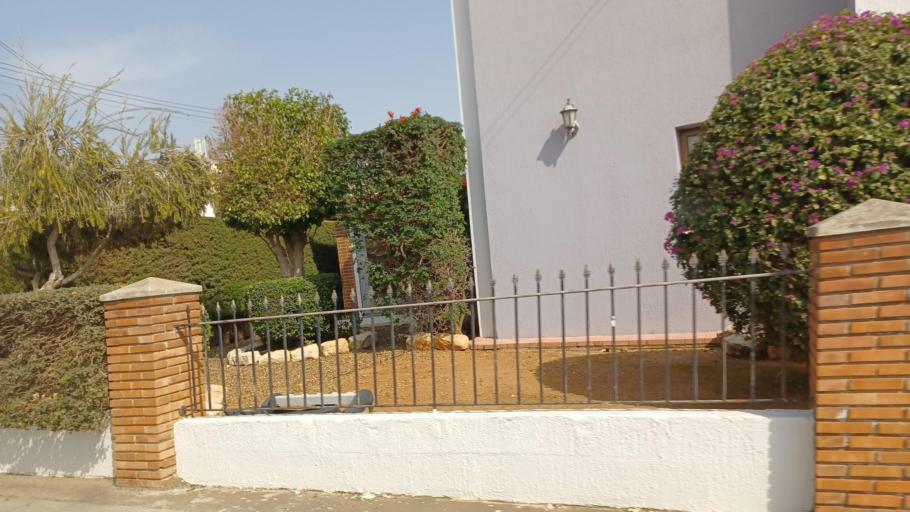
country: CY
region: Limassol
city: Ypsonas
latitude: 34.6878
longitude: 32.9672
